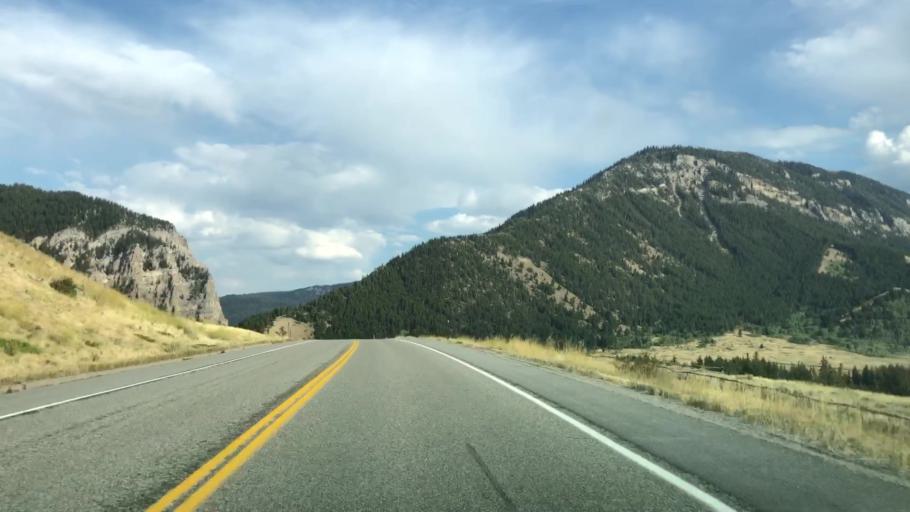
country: US
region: Wyoming
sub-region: Teton County
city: Hoback
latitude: 43.2909
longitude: -110.6505
